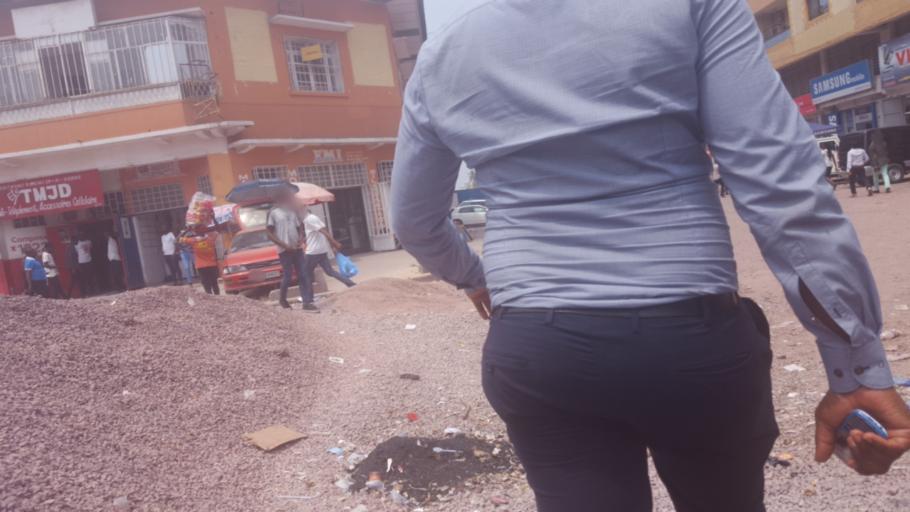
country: CD
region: Kinshasa
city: Kinshasa
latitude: -4.3052
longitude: 15.3113
